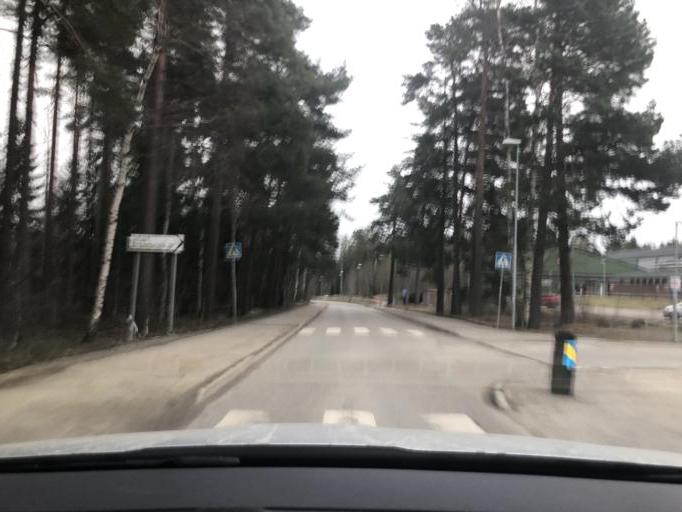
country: SE
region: Stockholm
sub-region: Botkyrka Kommun
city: Tullinge
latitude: 59.1933
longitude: 17.9035
